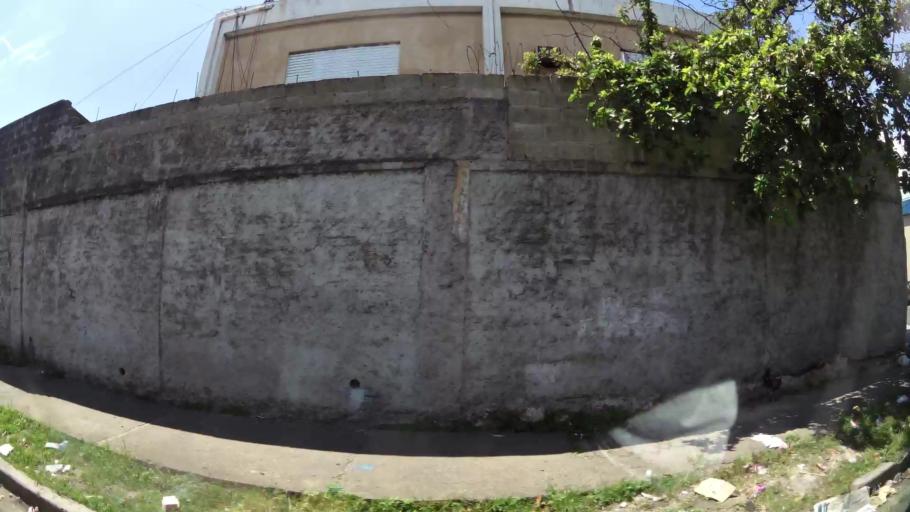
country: DO
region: Nacional
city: Ensanche Luperon
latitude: 18.4947
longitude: -69.8937
